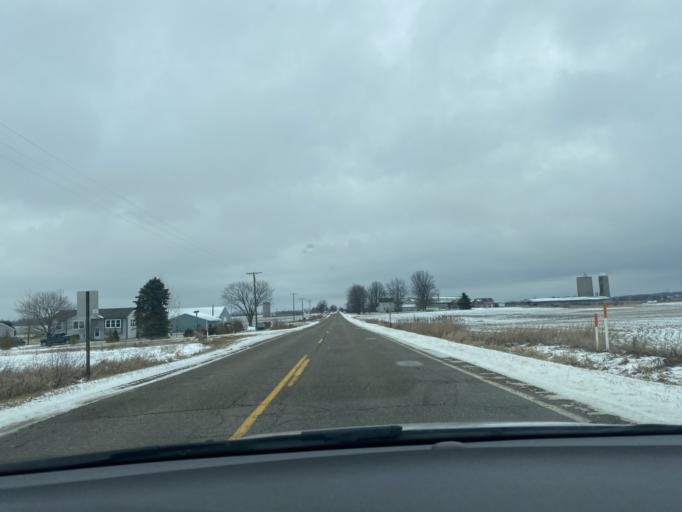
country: US
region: Michigan
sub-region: Lapeer County
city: North Branch
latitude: 43.2099
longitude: -83.1129
